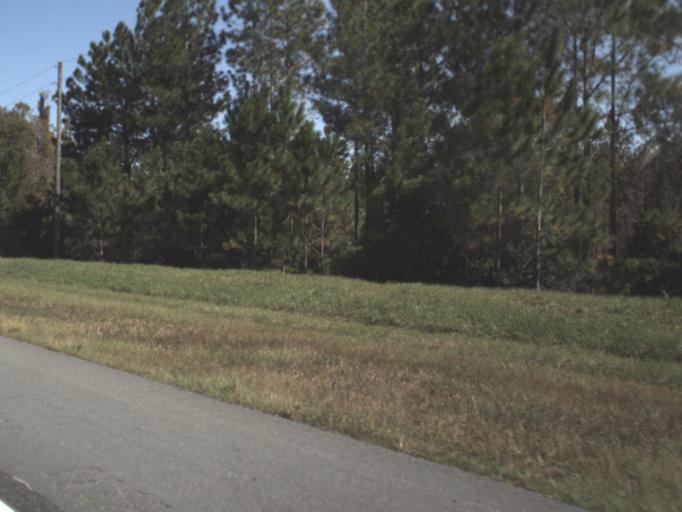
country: US
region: Florida
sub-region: Pasco County
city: Odessa
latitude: 28.2307
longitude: -82.5503
